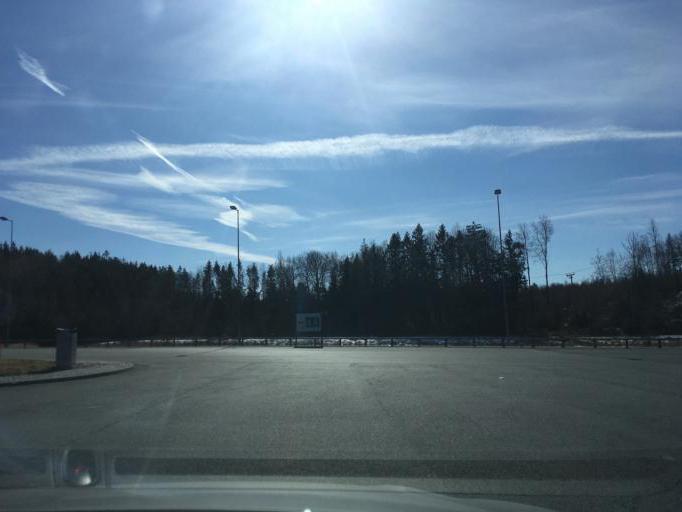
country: NO
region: Ostfold
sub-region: Sarpsborg
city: Skjeberg
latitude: 59.1081
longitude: 11.2621
